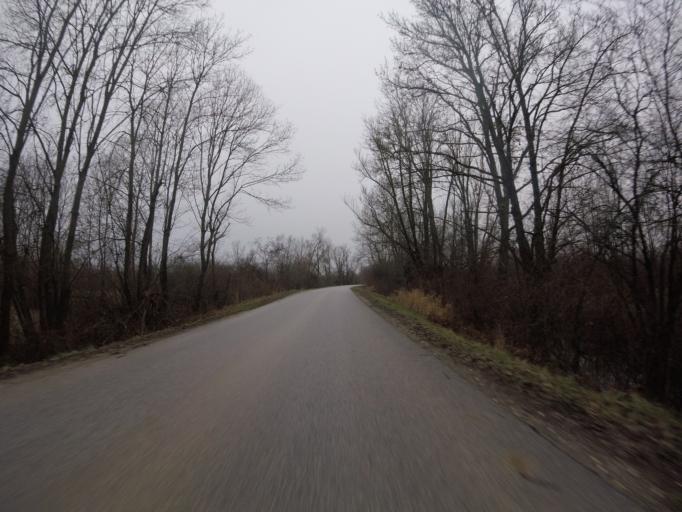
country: HR
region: Sisacko-Moslavacka
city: Lekenik
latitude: 45.6281
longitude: 16.3146
